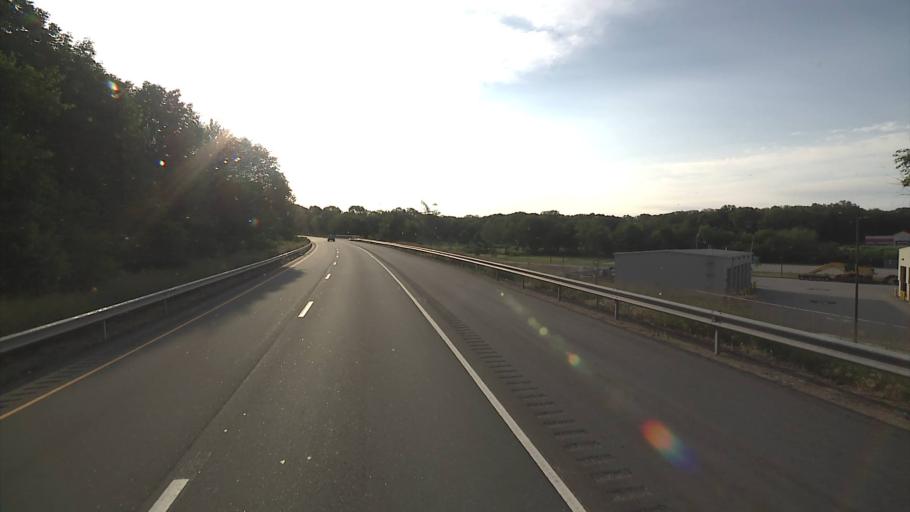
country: US
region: Connecticut
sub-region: New London County
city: Colchester
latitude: 41.5619
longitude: -72.3218
